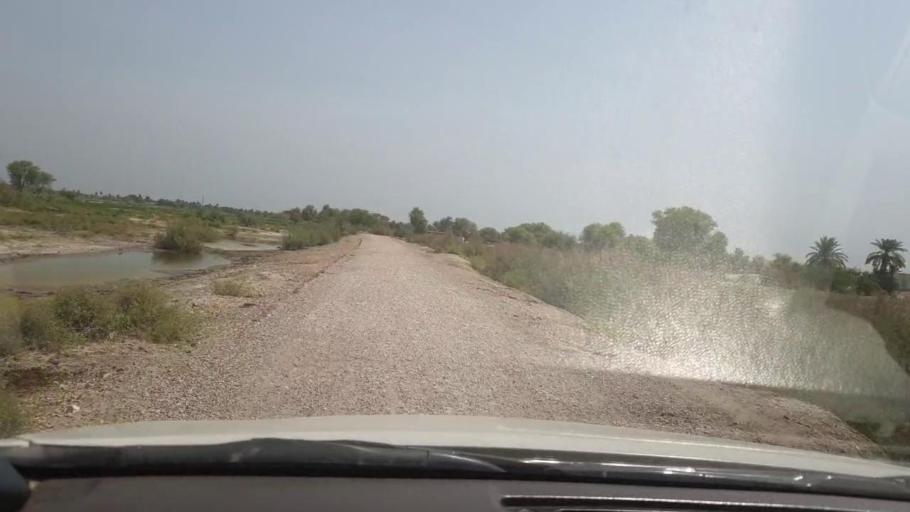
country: PK
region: Sindh
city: Shikarpur
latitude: 27.9273
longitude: 68.6048
